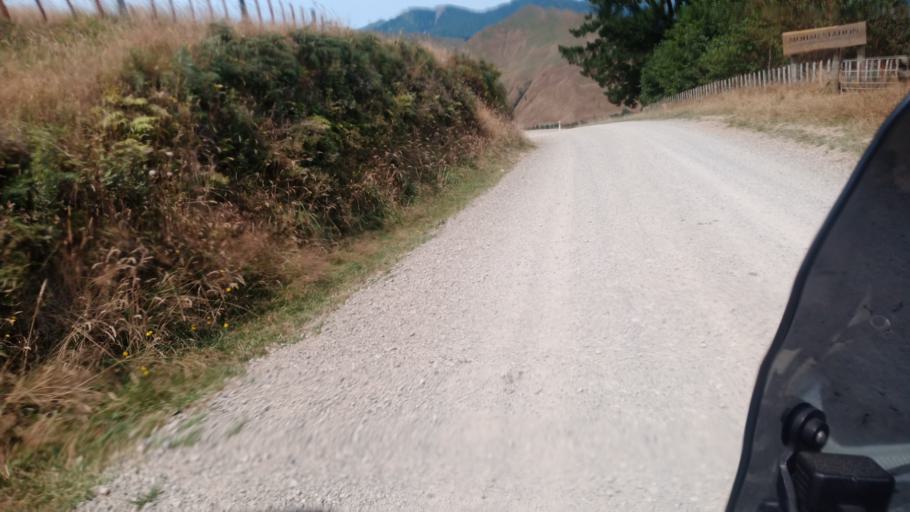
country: NZ
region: Bay of Plenty
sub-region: Opotiki District
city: Opotiki
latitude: -37.6560
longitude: 178.1285
